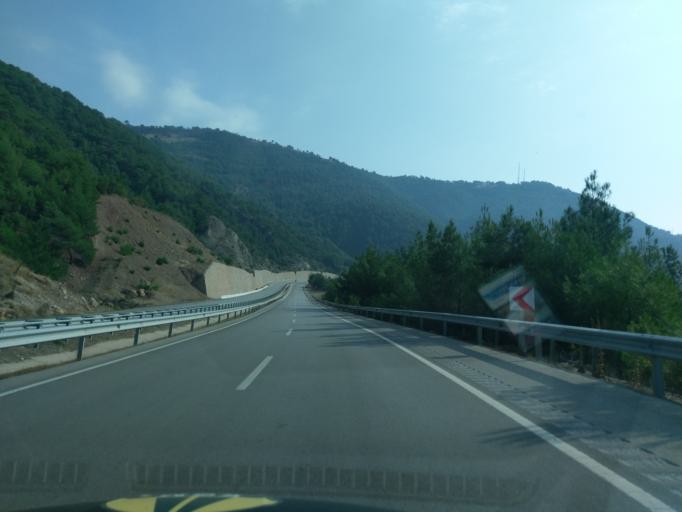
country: TR
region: Amasya
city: Akdag
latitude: 40.7519
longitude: 36.0792
